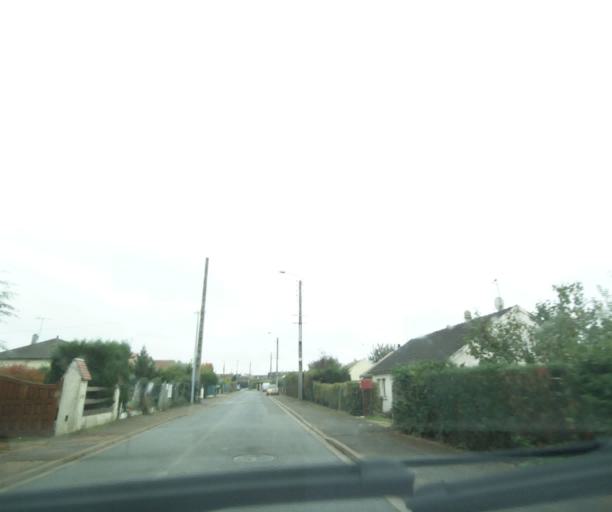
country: FR
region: Centre
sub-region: Departement d'Eure-et-Loir
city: Vernouillet
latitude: 48.7214
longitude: 1.3623
